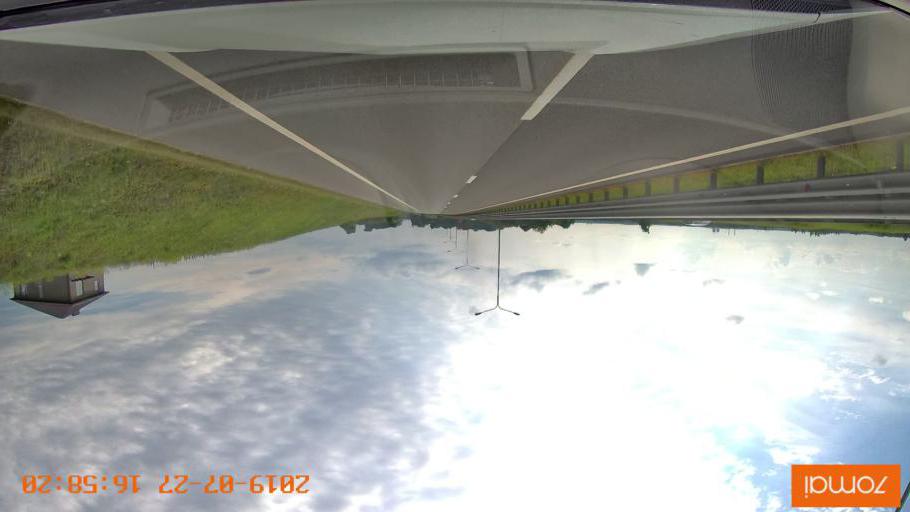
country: RU
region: Kaliningrad
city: Bol'shoe Isakovo
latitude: 54.7012
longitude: 20.6841
